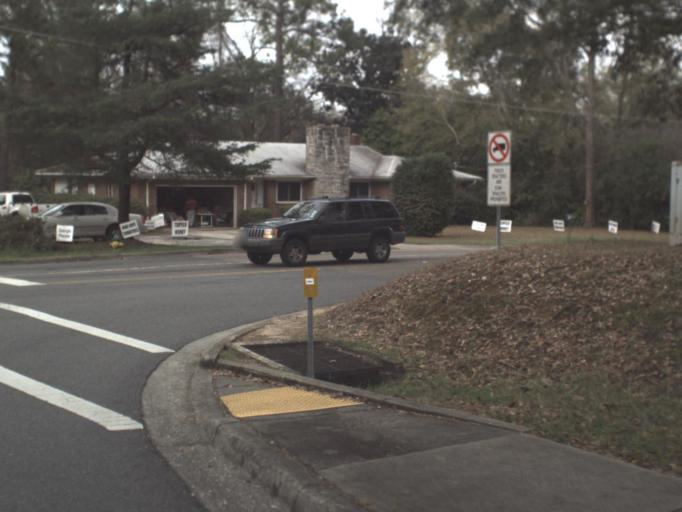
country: US
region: Florida
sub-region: Leon County
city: Tallahassee
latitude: 30.4649
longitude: -84.2772
